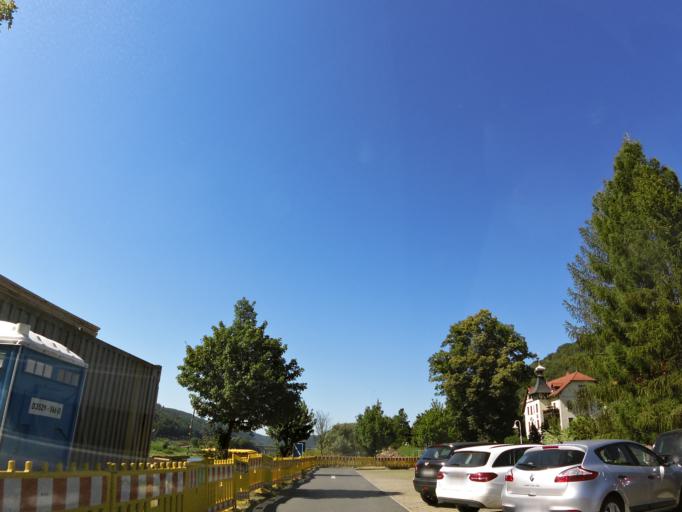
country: DE
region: Saxony
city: Bad Schandau
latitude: 50.9182
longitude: 14.1480
